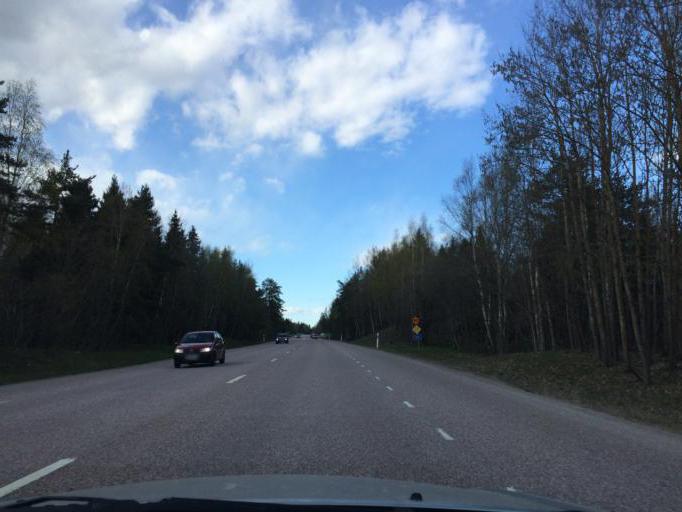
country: SE
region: Vaestmanland
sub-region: Hallstahammars Kommun
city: Kolback
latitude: 59.5755
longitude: 16.3526
